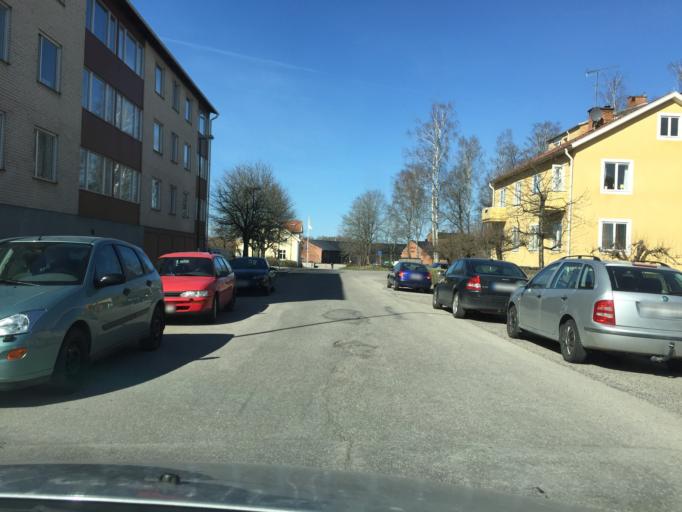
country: SE
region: Soedermanland
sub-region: Katrineholms Kommun
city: Katrineholm
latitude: 58.9943
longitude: 16.2190
